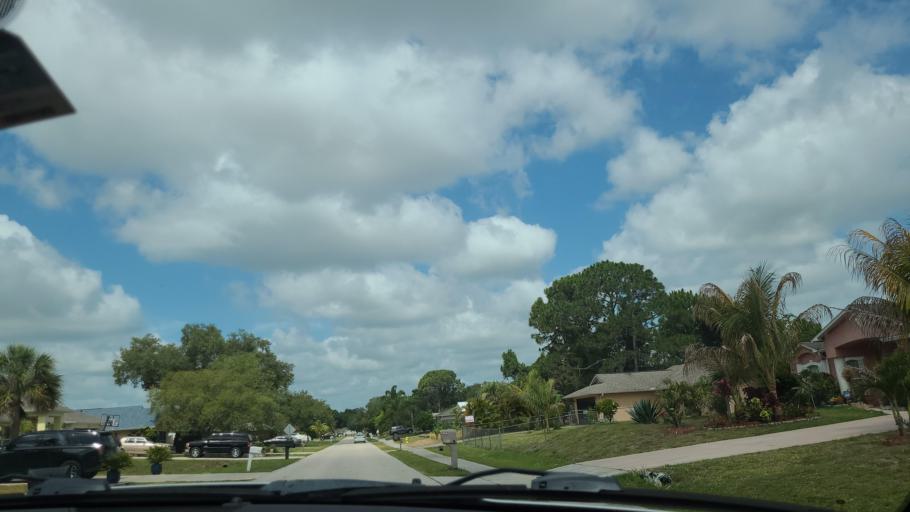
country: US
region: Florida
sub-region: Brevard County
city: Grant-Valkaria
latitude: 27.9691
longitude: -80.6500
